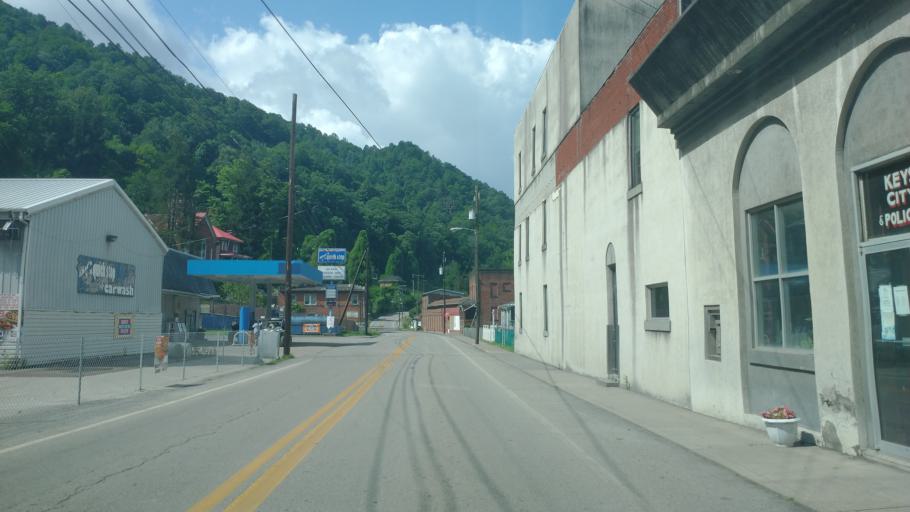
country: US
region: West Virginia
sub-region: McDowell County
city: Welch
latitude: 37.4149
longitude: -81.4508
